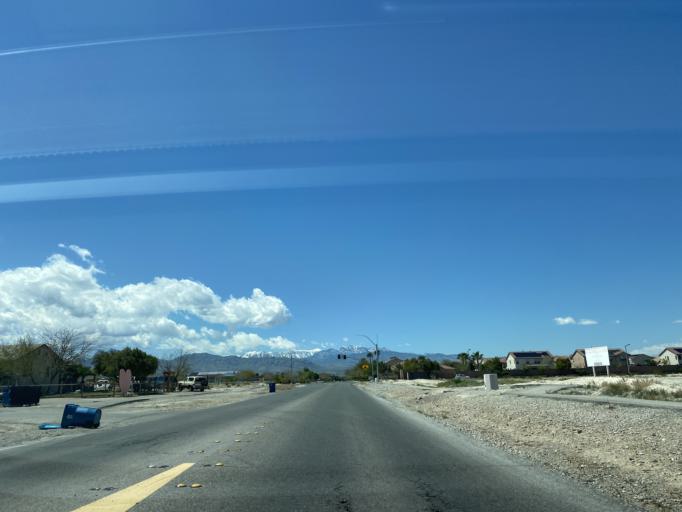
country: US
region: Nevada
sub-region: Clark County
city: North Las Vegas
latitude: 36.3131
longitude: -115.2137
